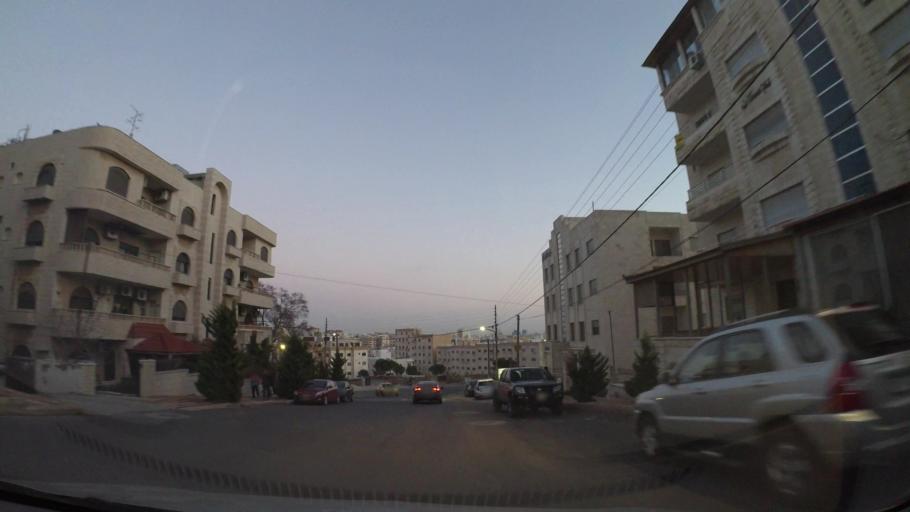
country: JO
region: Amman
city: Al Jubayhah
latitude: 31.9960
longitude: 35.8582
